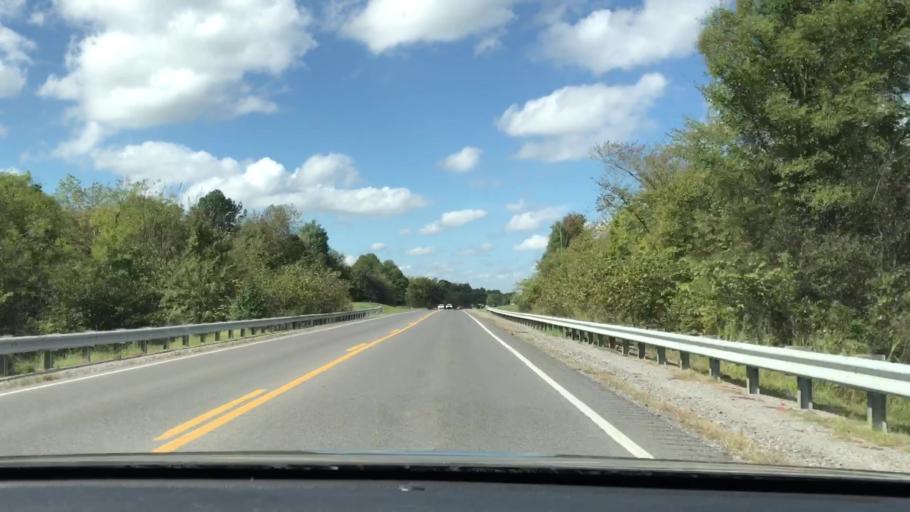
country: US
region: Kentucky
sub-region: McCracken County
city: Reidland
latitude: 37.0080
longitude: -88.4954
